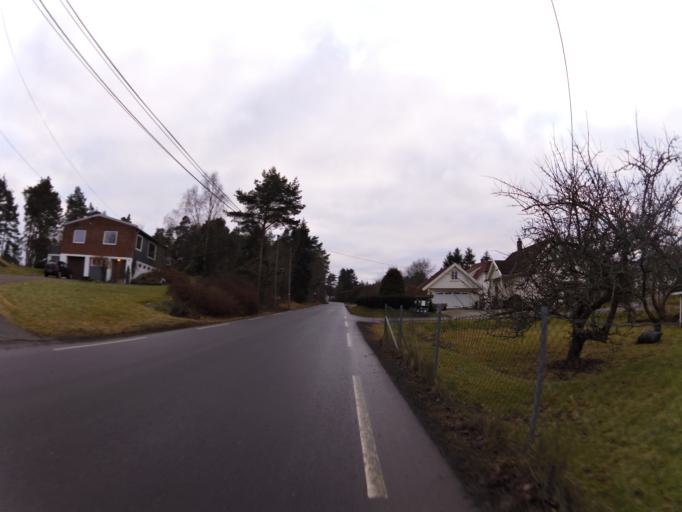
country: NO
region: Ostfold
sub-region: Fredrikstad
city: Fredrikstad
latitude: 59.1893
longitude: 10.8761
